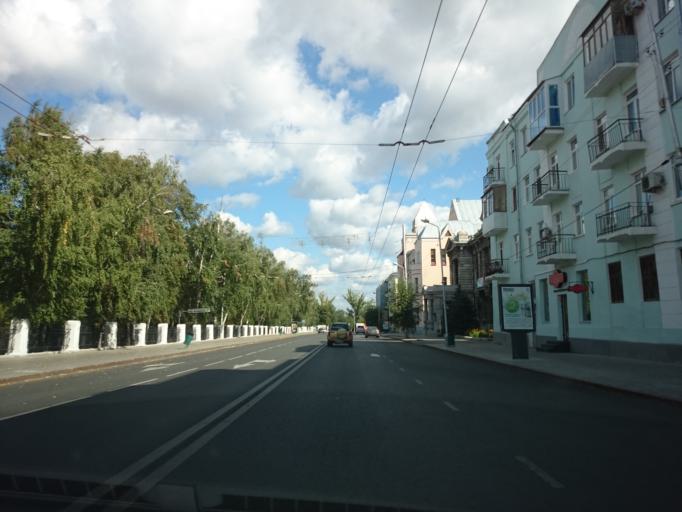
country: RU
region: Samara
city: Rozhdestveno
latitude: 53.1953
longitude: 50.0941
